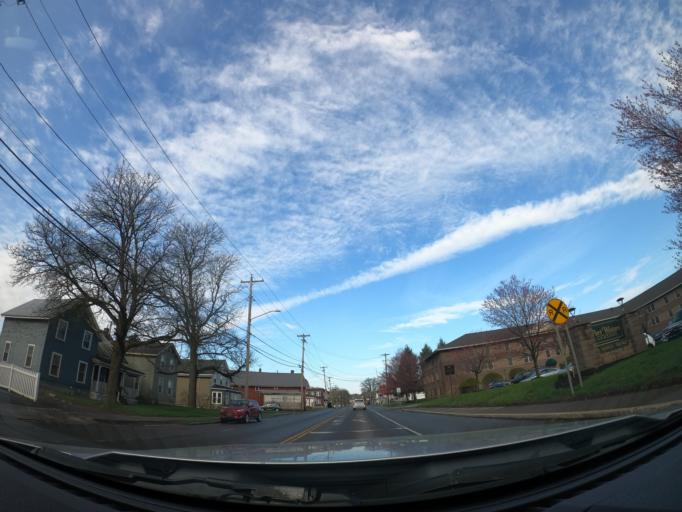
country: US
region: New York
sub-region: Cortland County
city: Cortland
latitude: 42.5981
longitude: -76.1698
